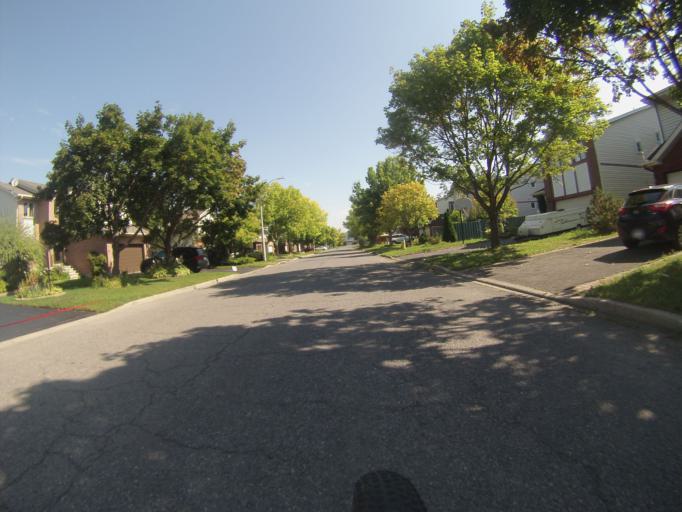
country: CA
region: Ontario
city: Ottawa
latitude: 45.3642
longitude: -75.6250
